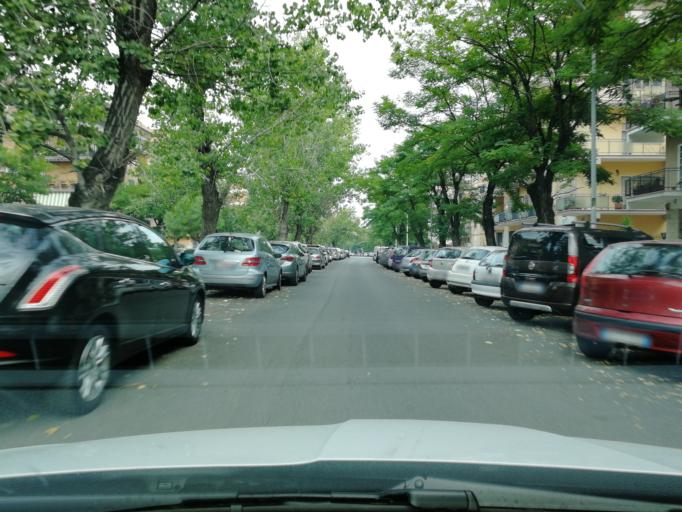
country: IT
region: Latium
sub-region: Citta metropolitana di Roma Capitale
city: Rome
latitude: 41.8508
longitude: 12.5642
